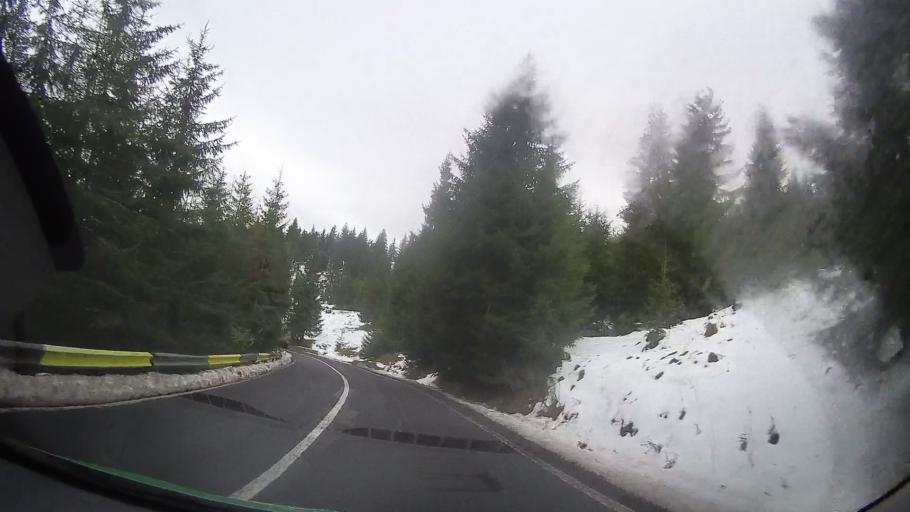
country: RO
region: Harghita
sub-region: Municipiul Gheorgheni
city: Gheorgheni
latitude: 46.7768
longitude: 25.7117
